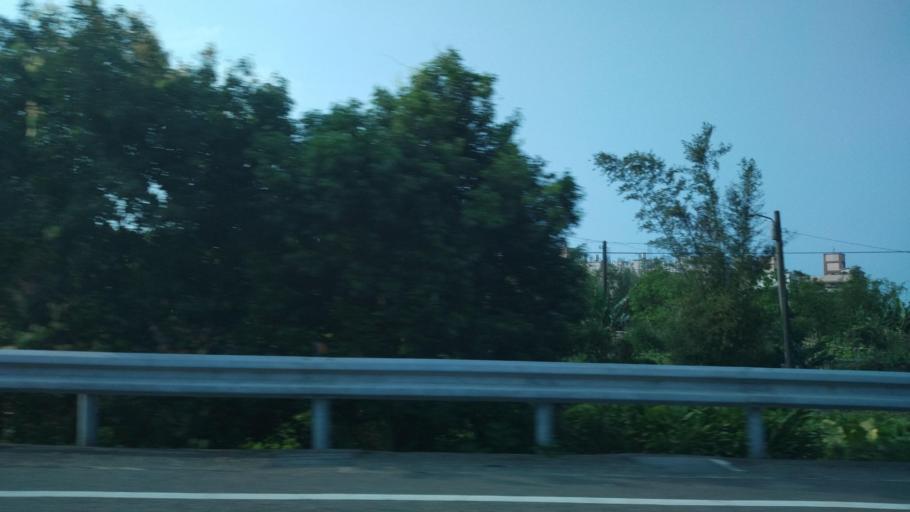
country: TW
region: Taiwan
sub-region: Keelung
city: Keelung
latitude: 25.2174
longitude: 121.6358
